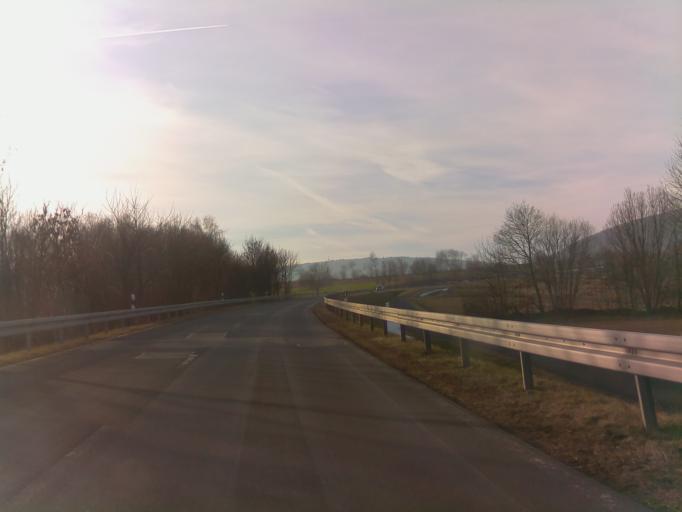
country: DE
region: Bavaria
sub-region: Regierungsbezirk Unterfranken
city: Sandberg
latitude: 50.3212
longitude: 9.9904
